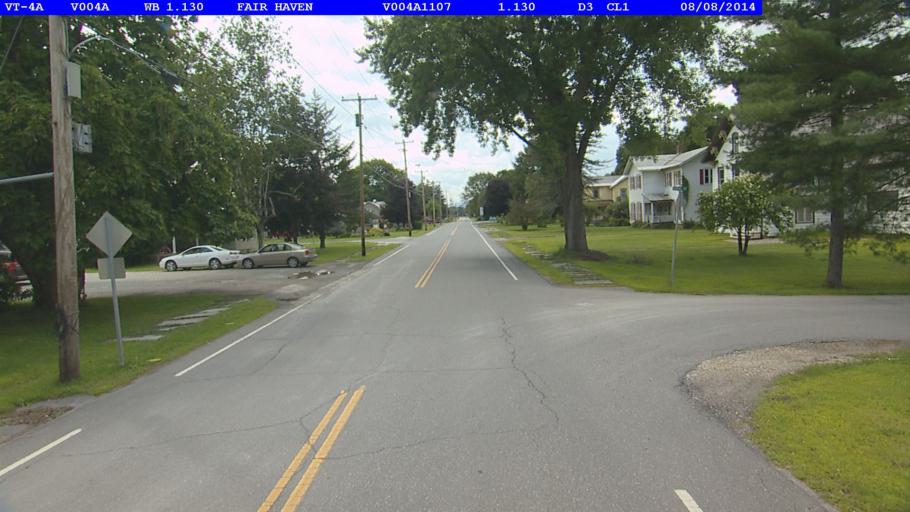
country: US
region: Vermont
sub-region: Rutland County
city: Fair Haven
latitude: 43.5874
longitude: -73.2714
